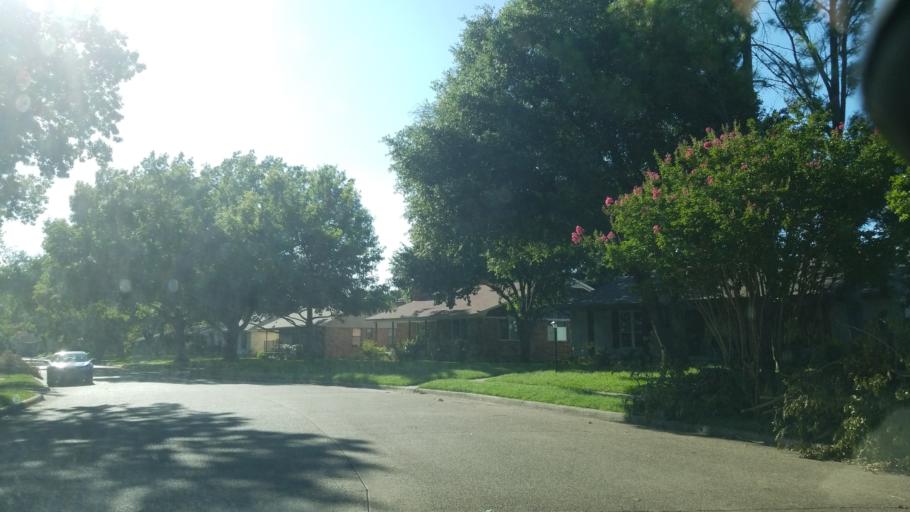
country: US
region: Texas
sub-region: Dallas County
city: Highland Park
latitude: 32.7895
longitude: -96.7032
